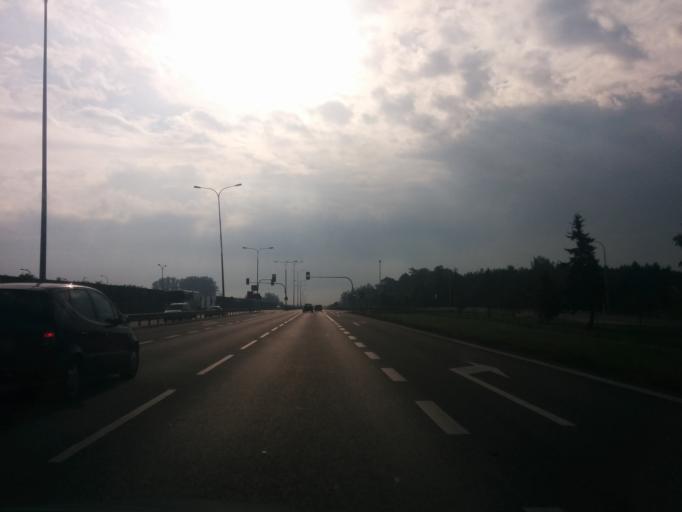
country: PL
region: Masovian Voivodeship
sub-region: Powiat radomski
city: Jedlinsk
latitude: 51.5317
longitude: 21.0815
